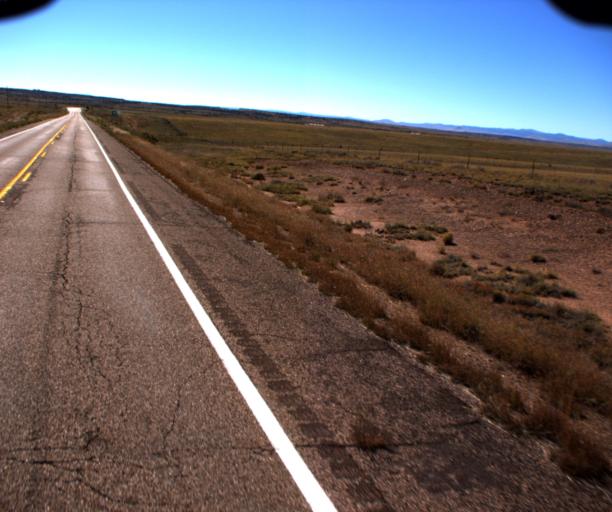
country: US
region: Arizona
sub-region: Apache County
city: Saint Johns
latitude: 34.5185
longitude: -109.4520
